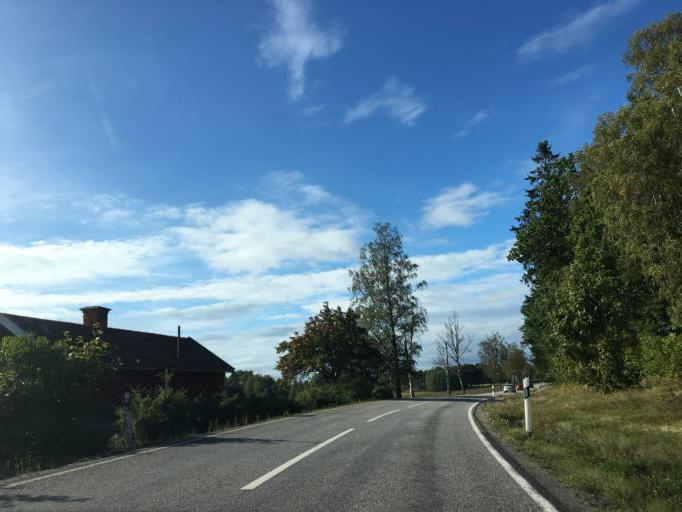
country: SE
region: Soedermanland
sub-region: Nykopings Kommun
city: Stigtomta
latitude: 58.8662
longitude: 16.9042
